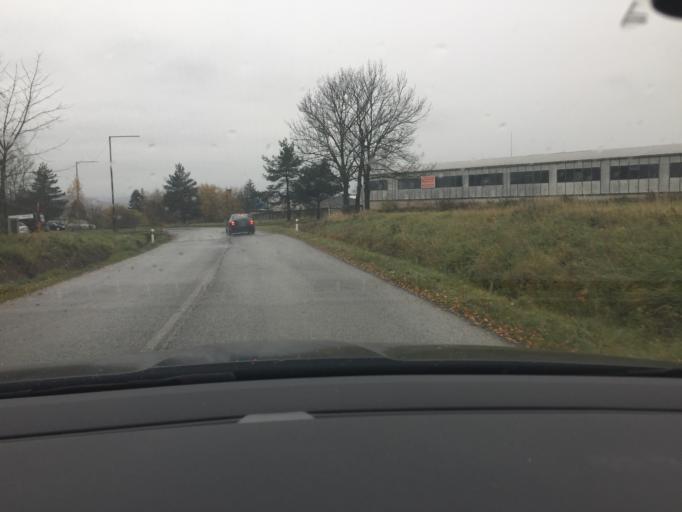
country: SK
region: Presovsky
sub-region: Okres Presov
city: Kezmarok
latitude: 49.1546
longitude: 20.4255
